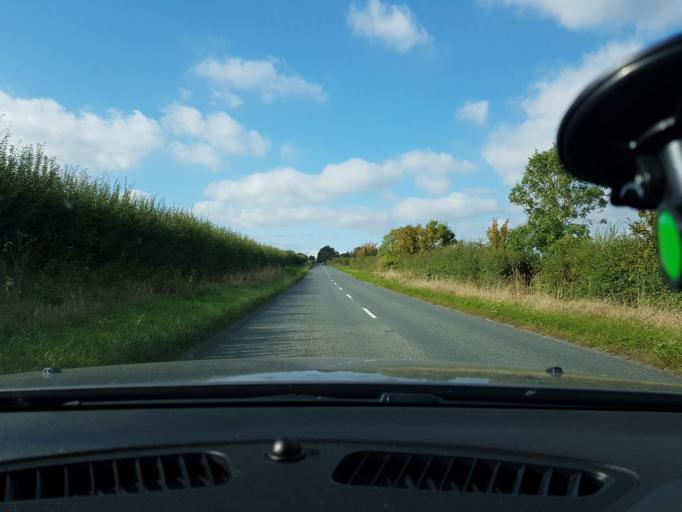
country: GB
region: England
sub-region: Wiltshire
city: Aldbourne
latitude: 51.4926
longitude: -1.6477
